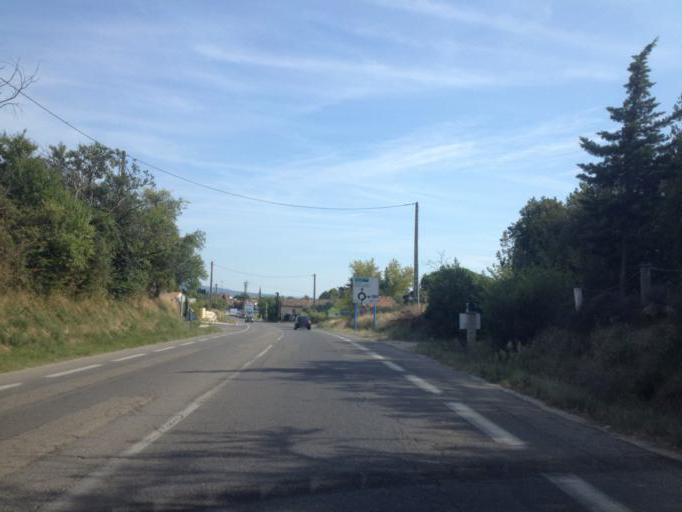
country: FR
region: Provence-Alpes-Cote d'Azur
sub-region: Departement du Vaucluse
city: Carpentras
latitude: 44.0690
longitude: 5.0429
